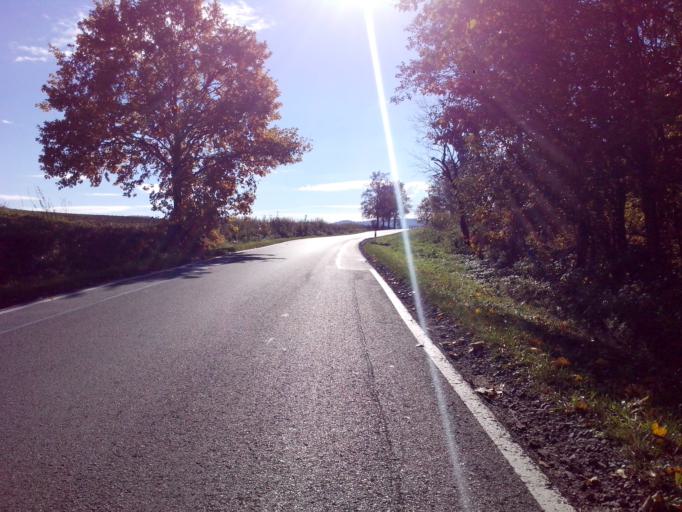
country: PL
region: Subcarpathian Voivodeship
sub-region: Powiat strzyzowski
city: Jawornik
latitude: 49.7988
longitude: 21.8631
